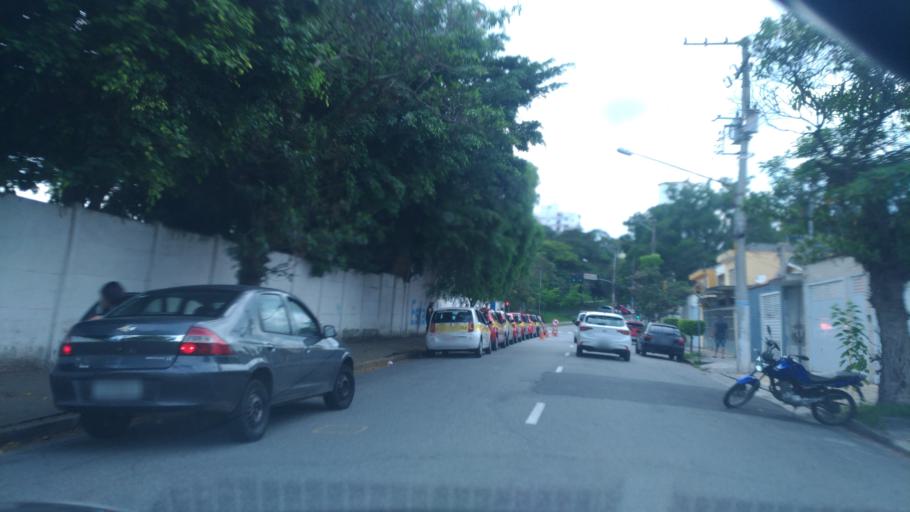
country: BR
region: Sao Paulo
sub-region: Sao Bernardo Do Campo
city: Sao Bernardo do Campo
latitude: -23.7070
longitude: -46.5426
